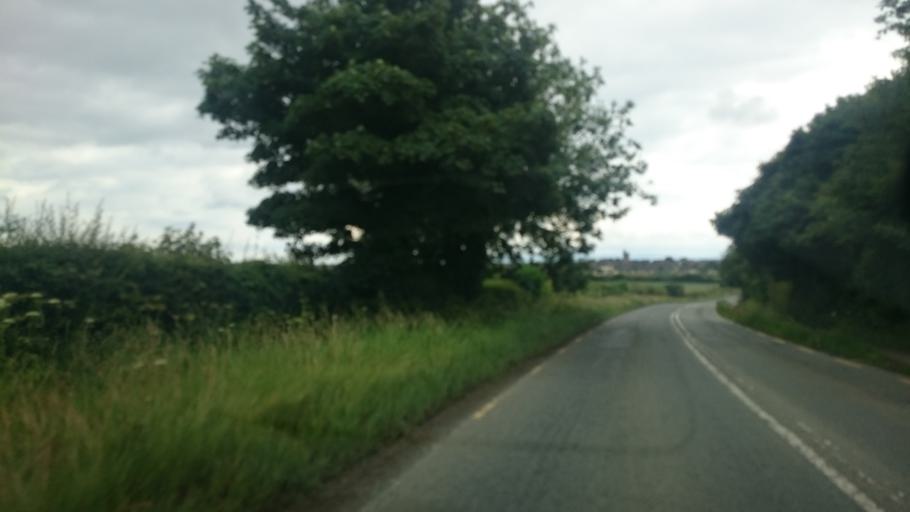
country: IE
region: Leinster
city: Lusk
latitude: 53.5351
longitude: -6.1615
